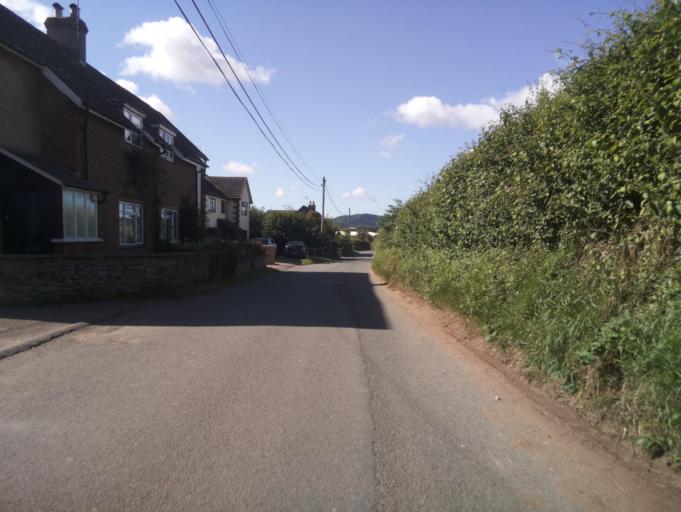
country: GB
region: England
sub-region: Herefordshire
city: Ross on Wye
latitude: 51.9331
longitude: -2.5778
